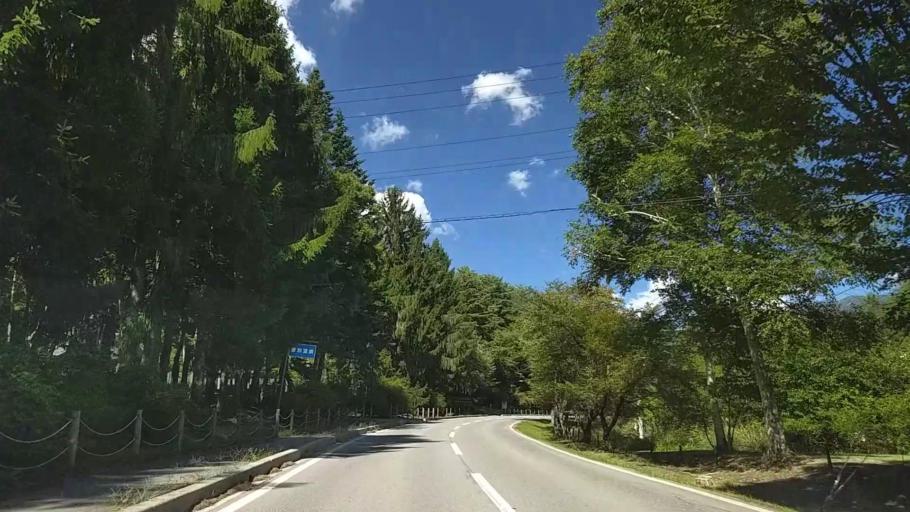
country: JP
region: Nagano
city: Chino
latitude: 36.0482
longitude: 138.2497
